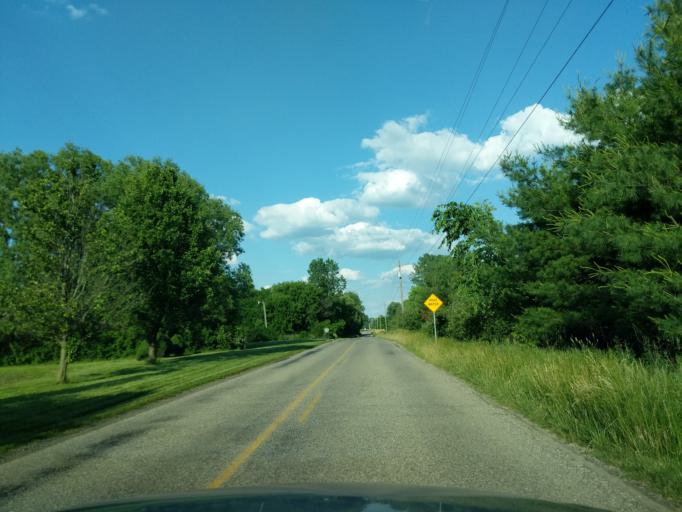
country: US
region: Indiana
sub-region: Whitley County
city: Tri-Lakes
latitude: 41.3021
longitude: -85.5163
